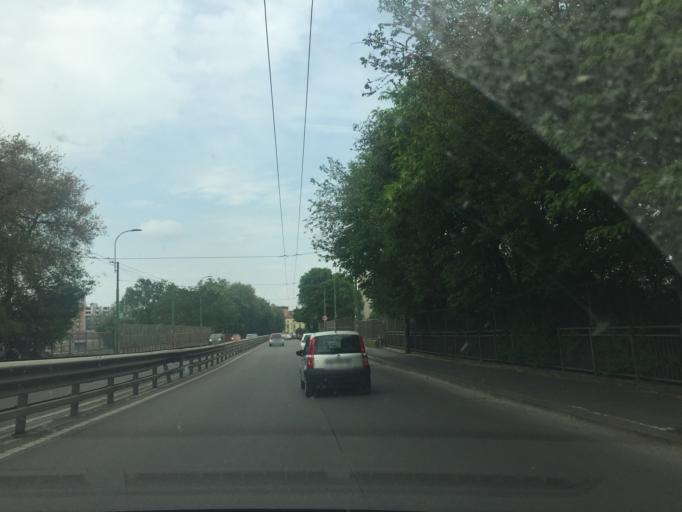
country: IT
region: Lombardy
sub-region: Citta metropolitana di Milano
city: Novate Milanese
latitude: 45.4963
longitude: 9.1612
